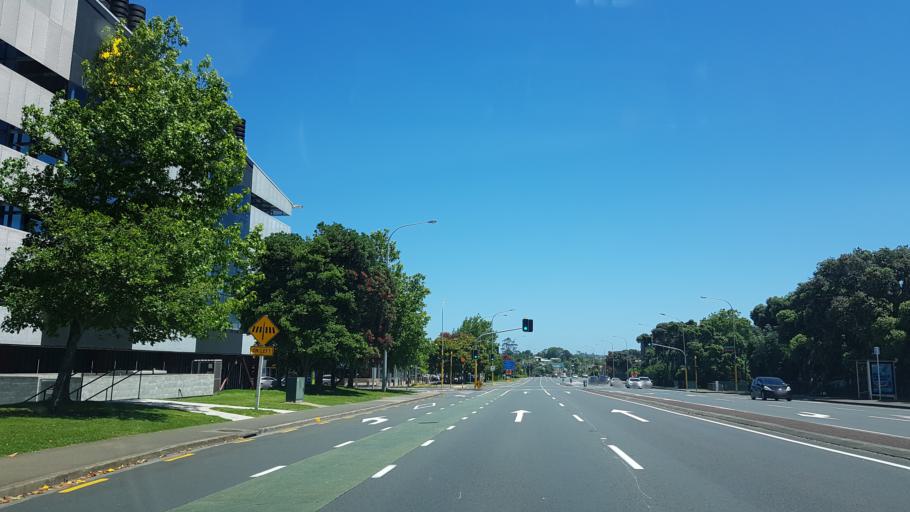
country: NZ
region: Auckland
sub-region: Auckland
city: North Shore
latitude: -36.7846
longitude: 174.7553
